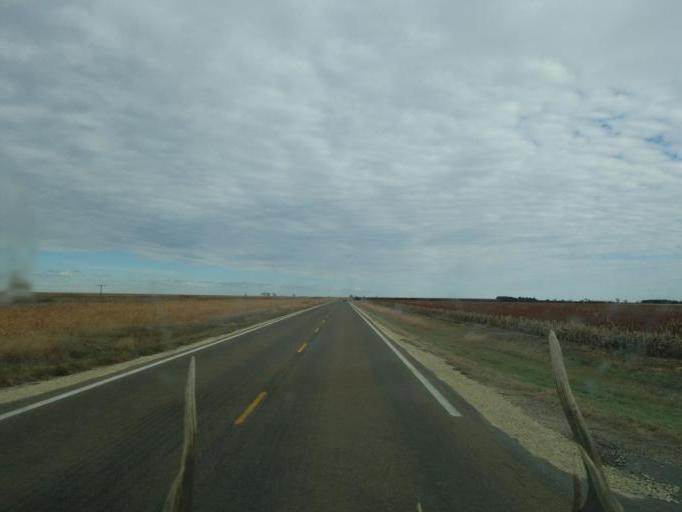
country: US
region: Kansas
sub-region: Logan County
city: Oakley
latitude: 39.0919
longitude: -101.1281
